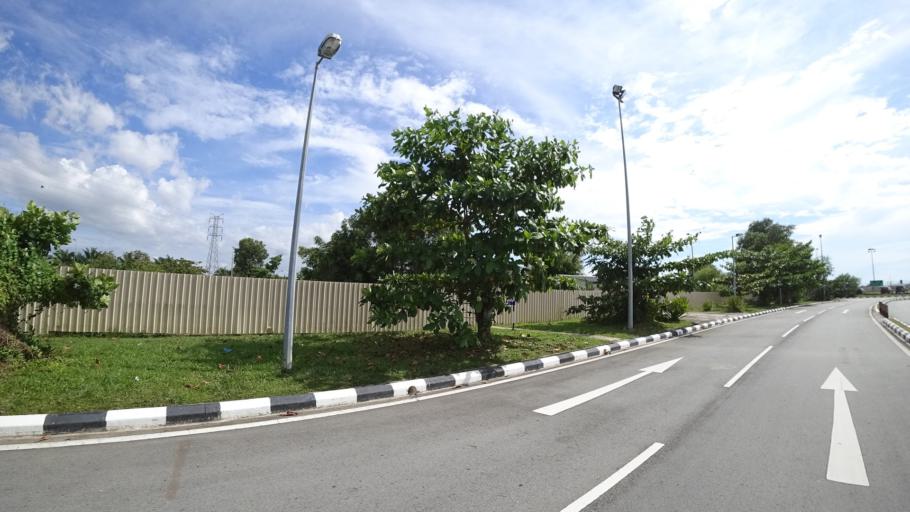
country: BN
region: Brunei and Muara
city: Bandar Seri Begawan
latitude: 4.9416
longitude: 114.9337
